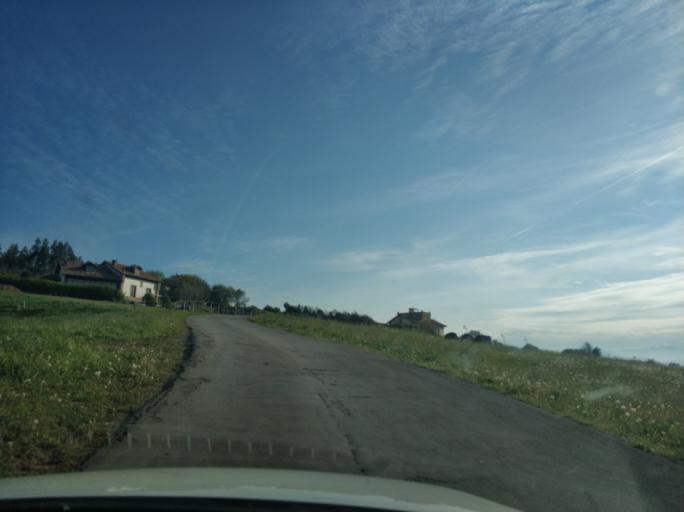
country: ES
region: Cantabria
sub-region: Provincia de Cantabria
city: Comillas
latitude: 43.3880
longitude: -4.3089
